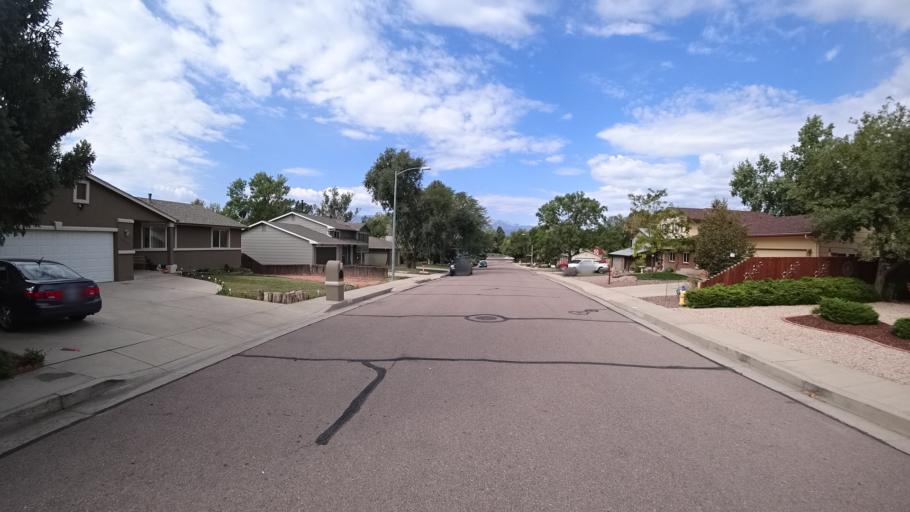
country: US
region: Colorado
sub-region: El Paso County
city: Cimarron Hills
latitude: 38.8489
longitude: -104.7276
